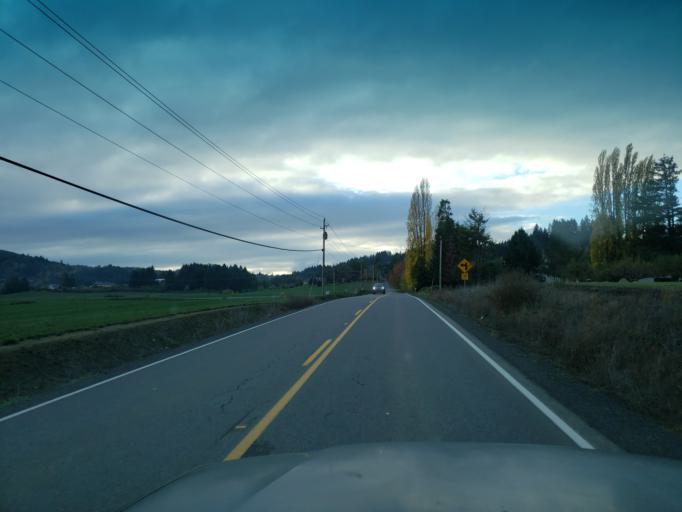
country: US
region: Oregon
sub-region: Yamhill County
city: McMinnville
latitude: 45.2305
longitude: -123.2504
